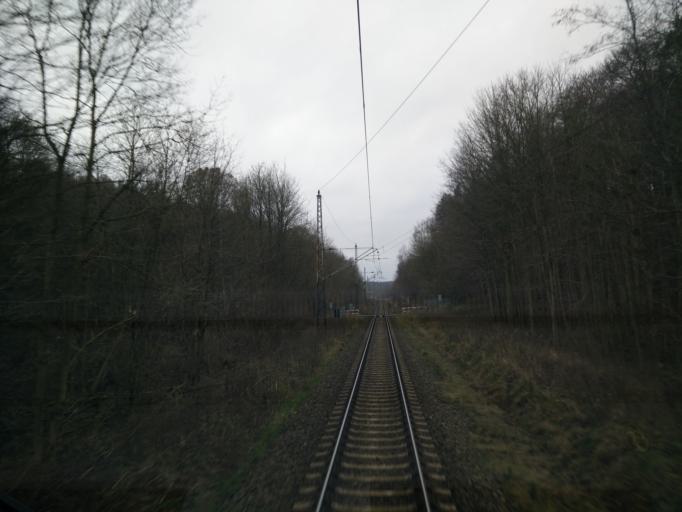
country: DE
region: Mecklenburg-Vorpommern
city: Bad Kleinen
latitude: 53.8024
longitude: 11.4834
